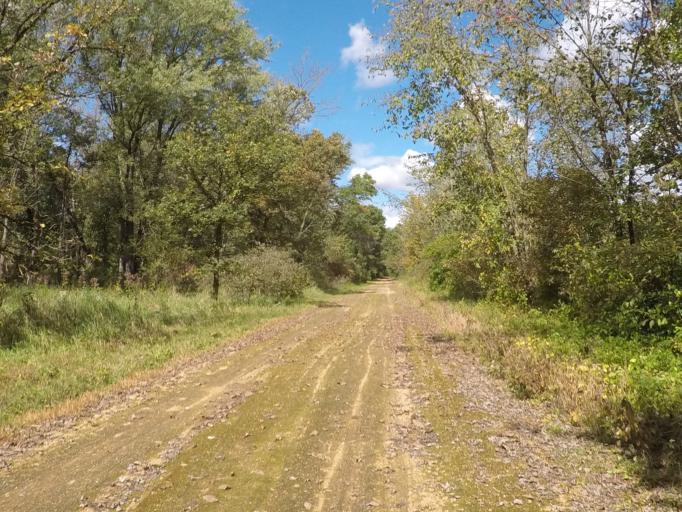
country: US
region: Wisconsin
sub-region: Richland County
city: Richland Center
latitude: 43.2876
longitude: -90.3227
